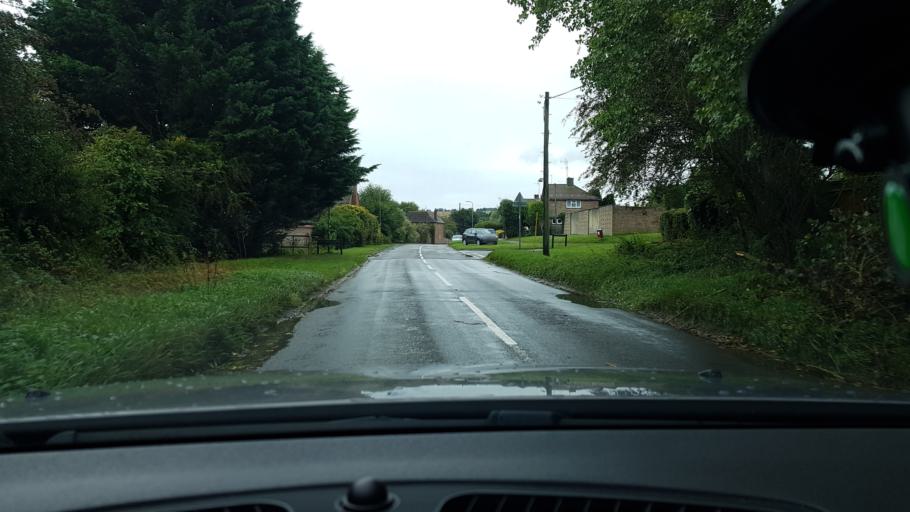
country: GB
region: England
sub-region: West Berkshire
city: Lambourn
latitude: 51.5126
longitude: -1.5245
